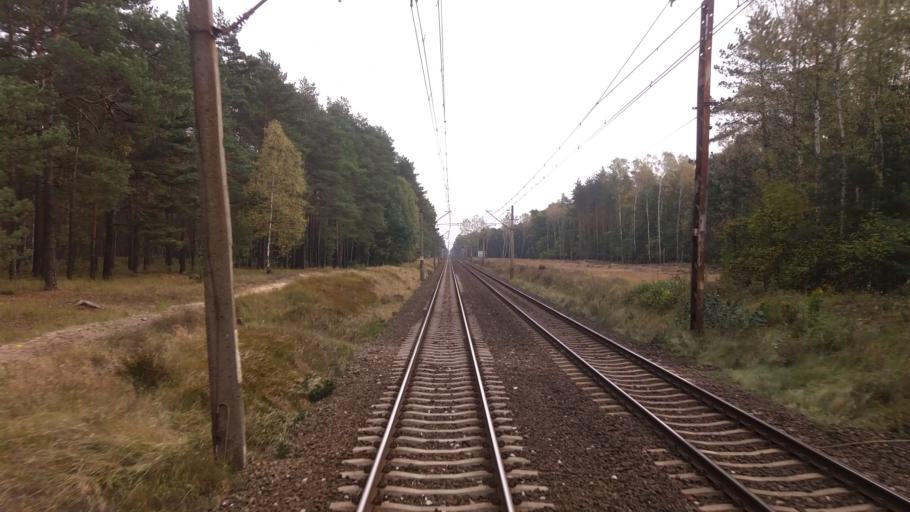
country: PL
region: West Pomeranian Voivodeship
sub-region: Powiat stargardzki
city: Kobylanka
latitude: 53.3795
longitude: 14.7979
